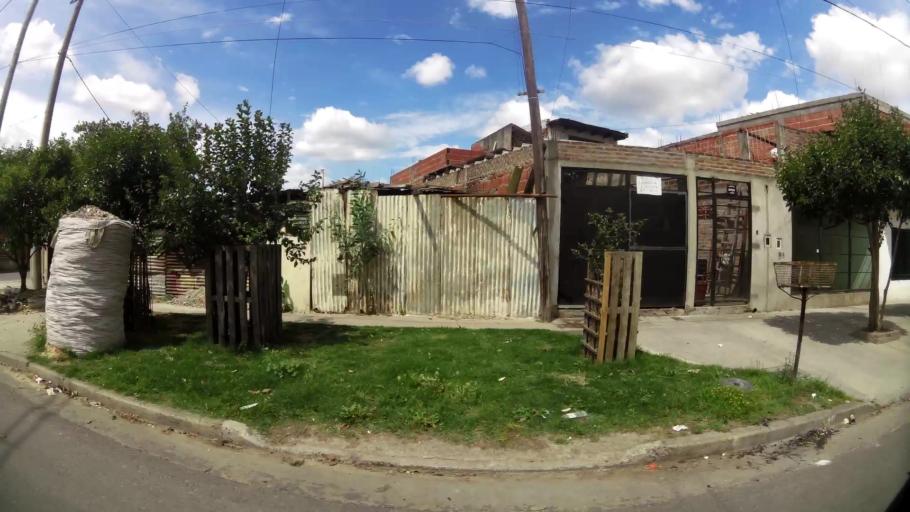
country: AR
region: Santa Fe
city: Gobernador Galvez
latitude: -33.0126
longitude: -60.6382
